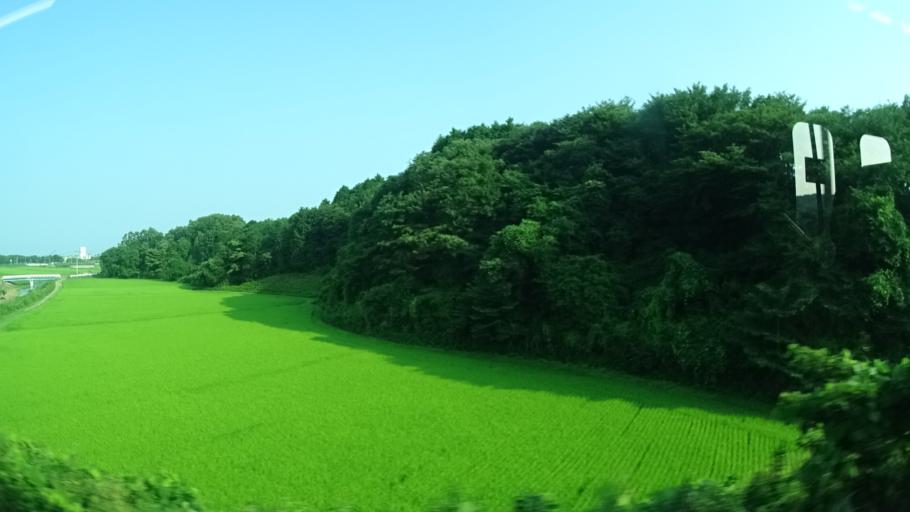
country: JP
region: Ibaraki
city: Takahagi
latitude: 36.6874
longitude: 140.7038
